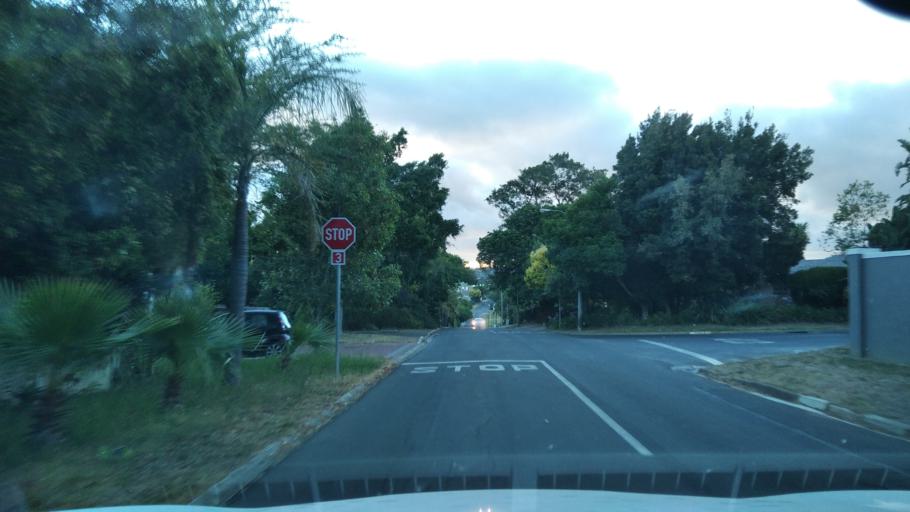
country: ZA
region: Western Cape
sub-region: City of Cape Town
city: Kraaifontein
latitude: -33.8217
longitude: 18.6583
